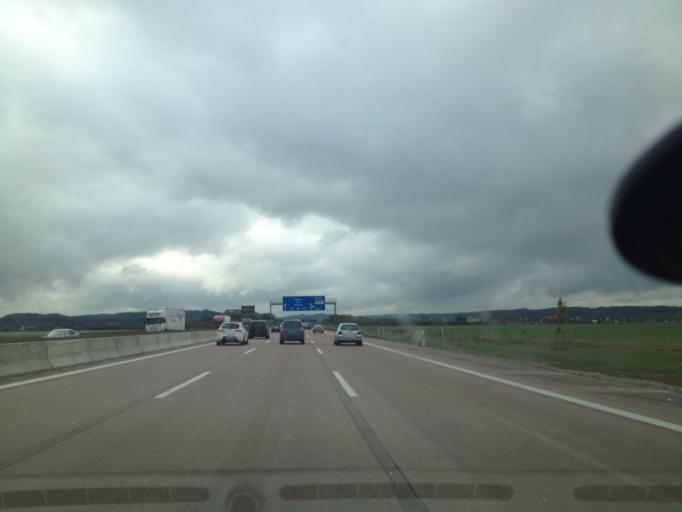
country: DE
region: Bavaria
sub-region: Swabia
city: Gersthofen
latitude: 48.4163
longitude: 10.8490
